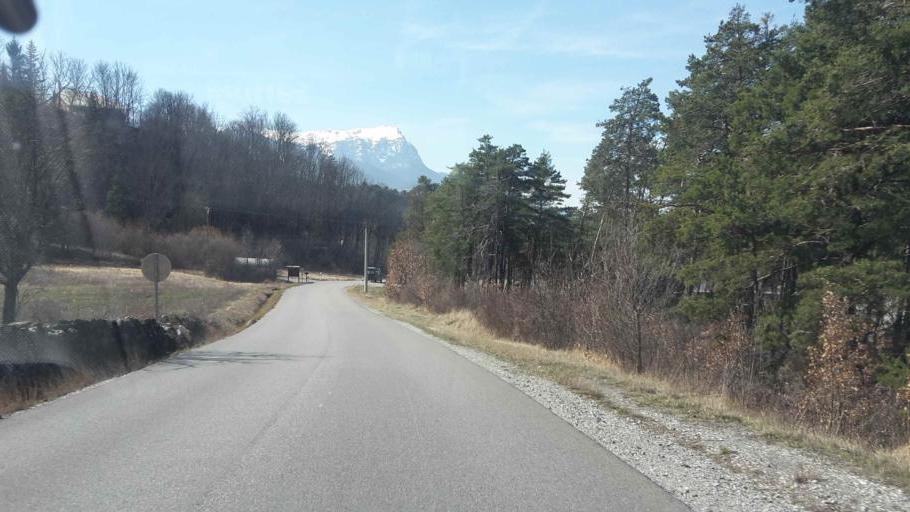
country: FR
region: Provence-Alpes-Cote d'Azur
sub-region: Departement des Hautes-Alpes
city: Embrun
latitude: 44.5636
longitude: 6.5186
